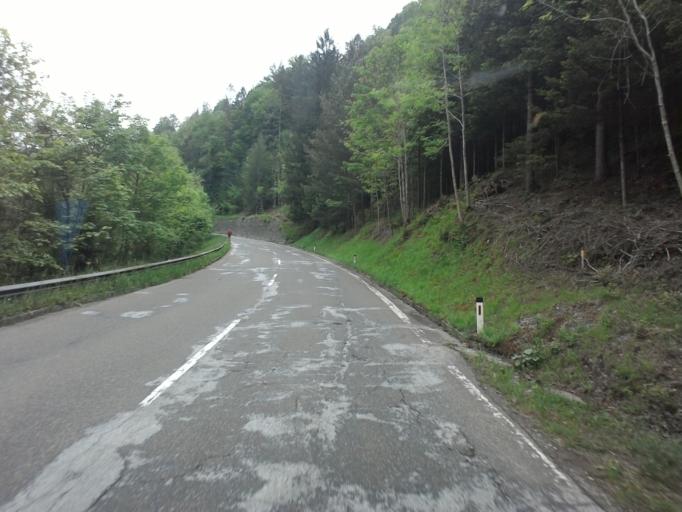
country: AT
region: Styria
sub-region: Politischer Bezirk Liezen
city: Landl
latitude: 47.6725
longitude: 14.7139
